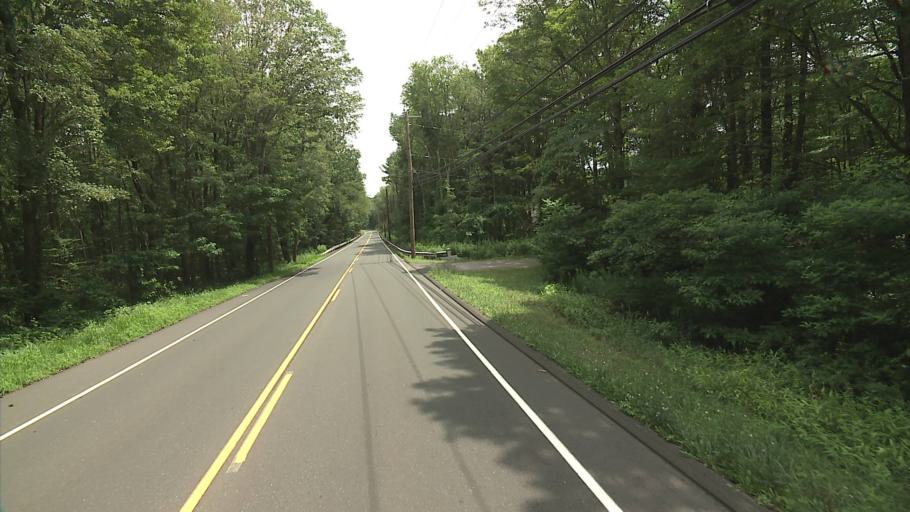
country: US
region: Connecticut
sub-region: New Haven County
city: Madison Center
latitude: 41.3584
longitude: -72.6218
